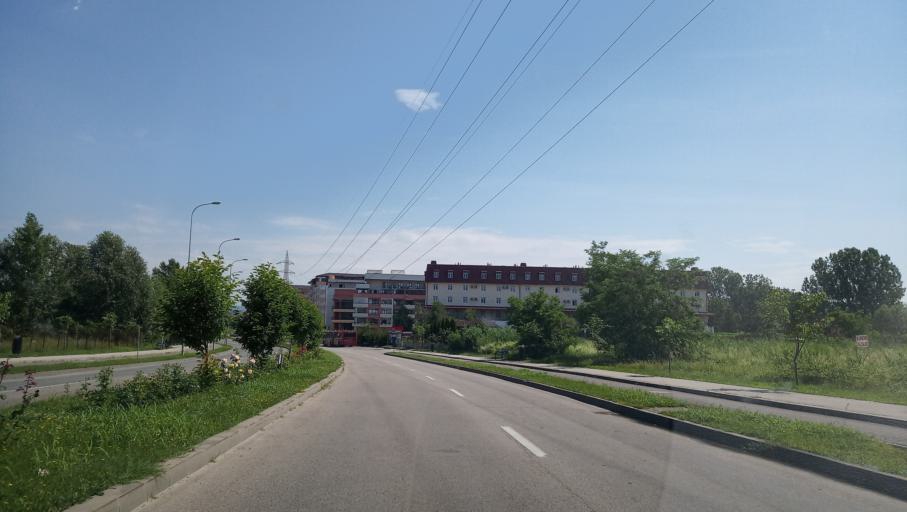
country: RO
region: Valcea
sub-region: Municipiul Ramnicu Valcea
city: Ramnicu Valcea
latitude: 45.0808
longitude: 24.3658
